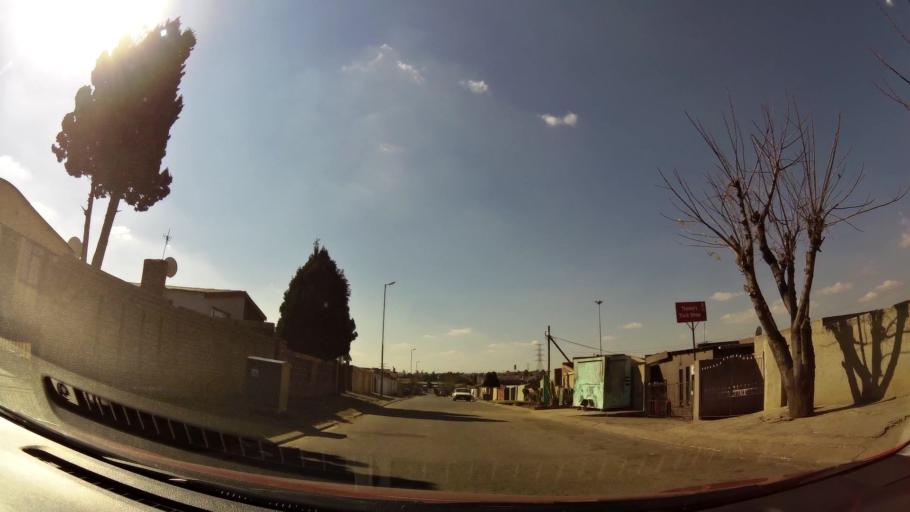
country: ZA
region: Gauteng
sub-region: City of Johannesburg Metropolitan Municipality
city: Soweto
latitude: -26.2454
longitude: 27.9038
